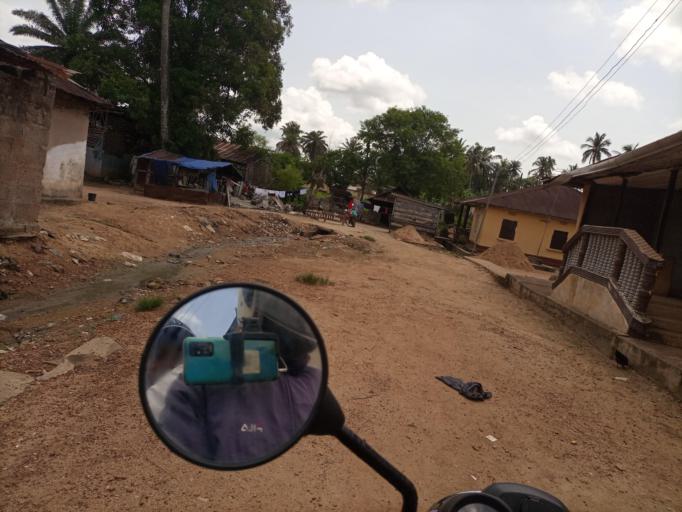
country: SL
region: Southern Province
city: Bo
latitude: 7.9588
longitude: -11.7359
